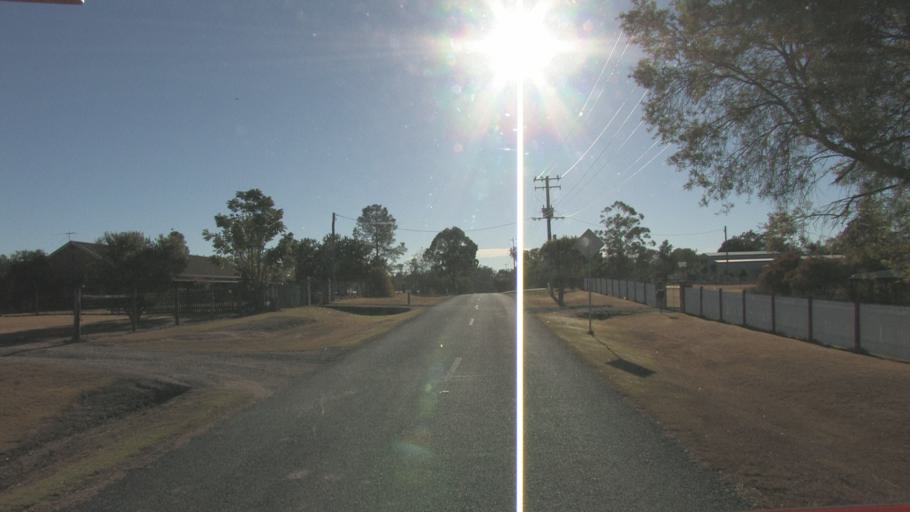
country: AU
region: Queensland
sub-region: Logan
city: North Maclean
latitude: -27.7996
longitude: 153.0052
